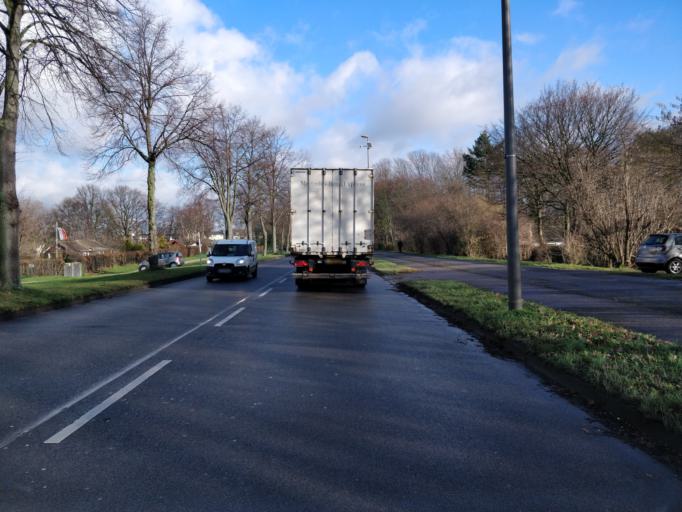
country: DE
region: North Rhine-Westphalia
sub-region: Regierungsbezirk Koln
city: Bilderstoeckchen
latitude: 50.9615
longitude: 6.9081
